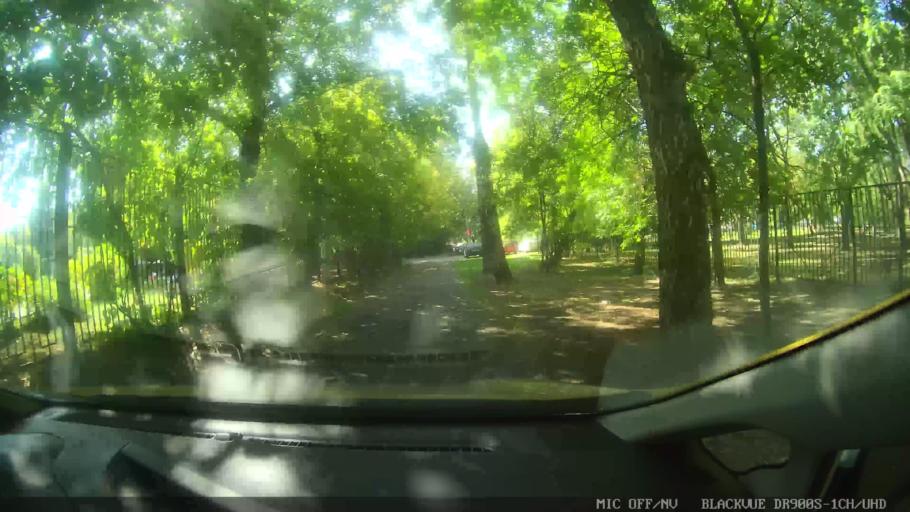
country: RU
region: Moscow
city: Kuz'minki
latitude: 55.7001
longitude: 37.7881
